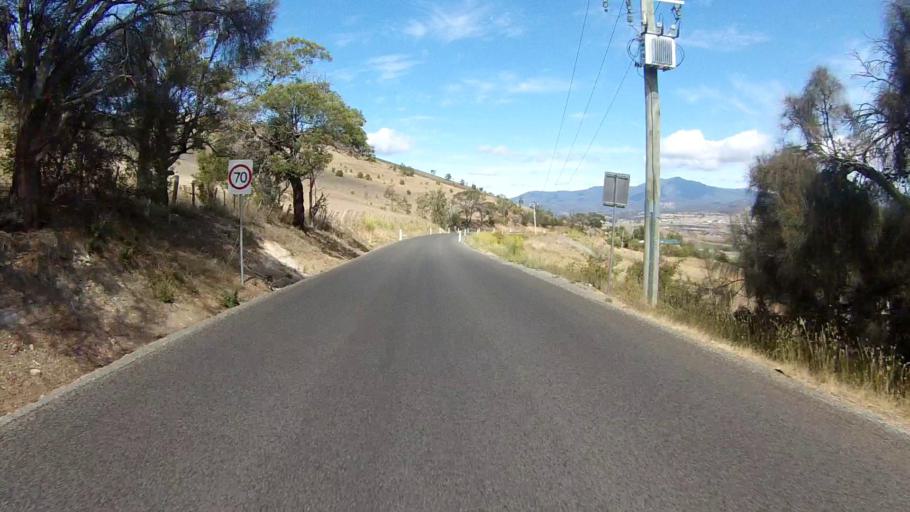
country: AU
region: Tasmania
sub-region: Glenorchy
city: Austins Ferry
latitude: -42.7285
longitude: 147.2760
